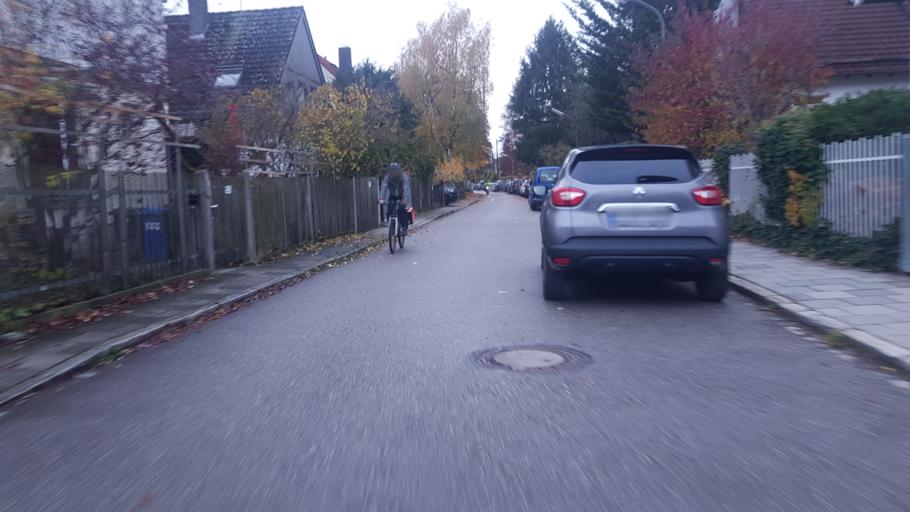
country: DE
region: Bavaria
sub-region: Upper Bavaria
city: Pasing
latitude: 48.1561
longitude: 11.4768
